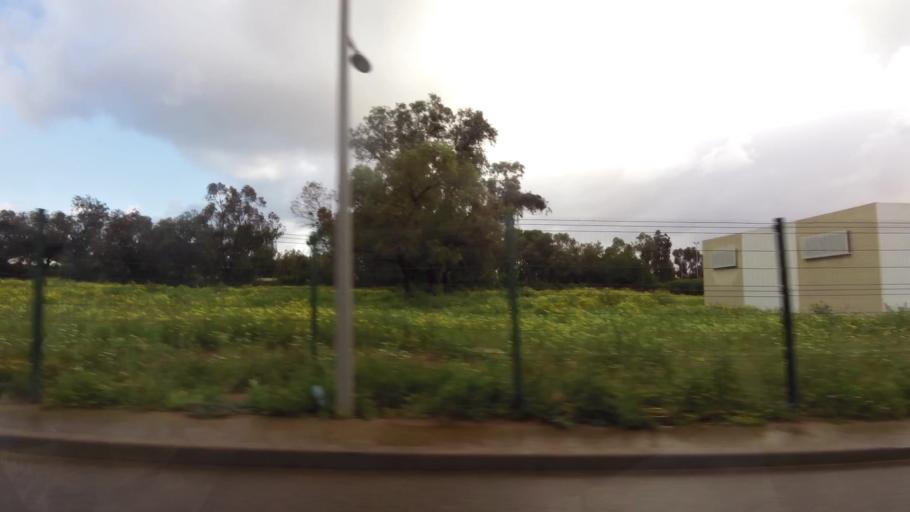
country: MA
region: Grand Casablanca
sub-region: Casablanca
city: Casablanca
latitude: 33.5616
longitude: -7.6518
